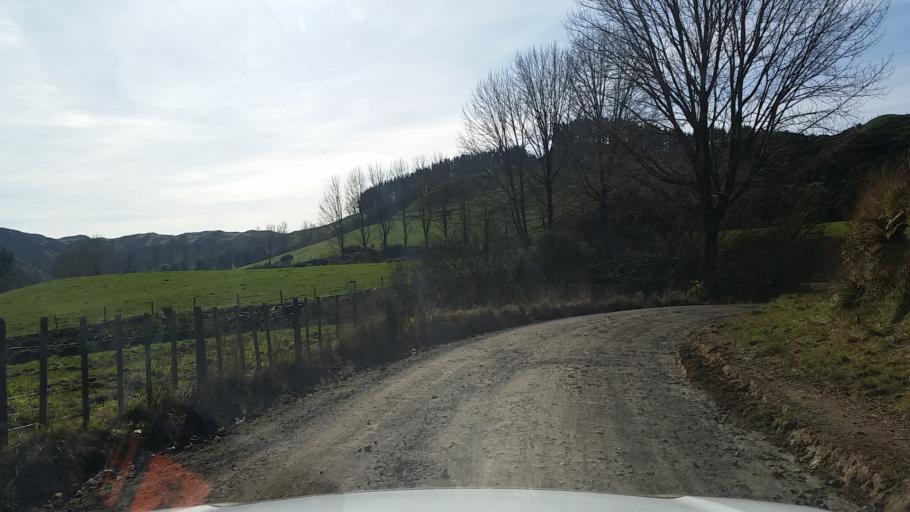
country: NZ
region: Taranaki
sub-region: South Taranaki District
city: Eltham
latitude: -39.3554
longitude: 174.5130
